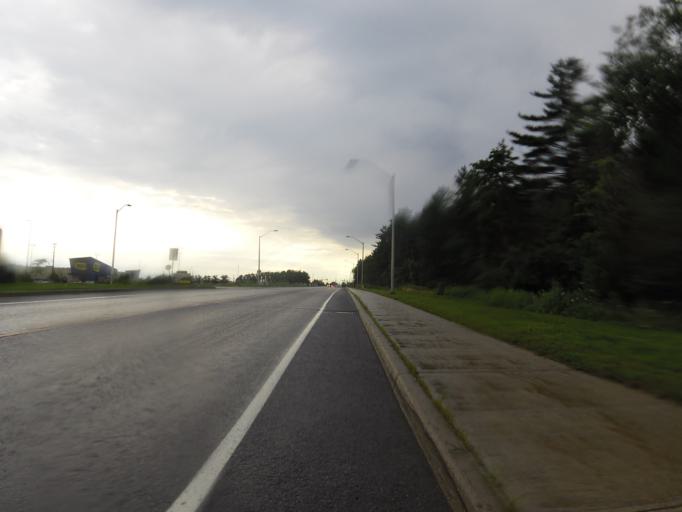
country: CA
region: Ontario
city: Bells Corners
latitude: 45.3122
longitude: -75.9071
